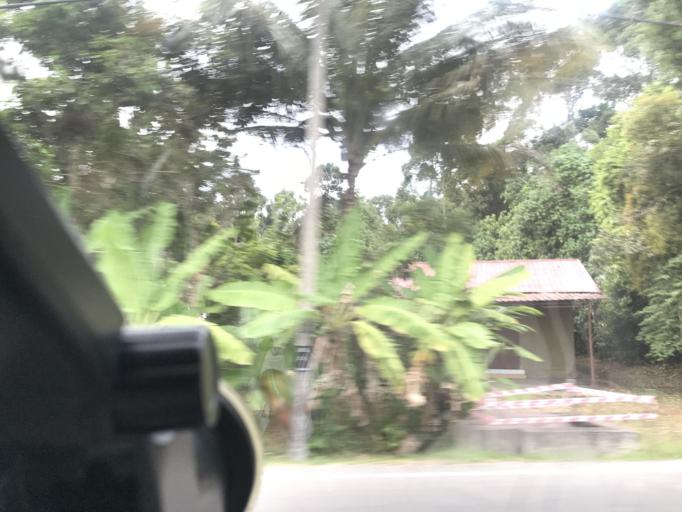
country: MY
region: Kelantan
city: Kota Bharu
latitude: 6.1260
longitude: 102.1748
